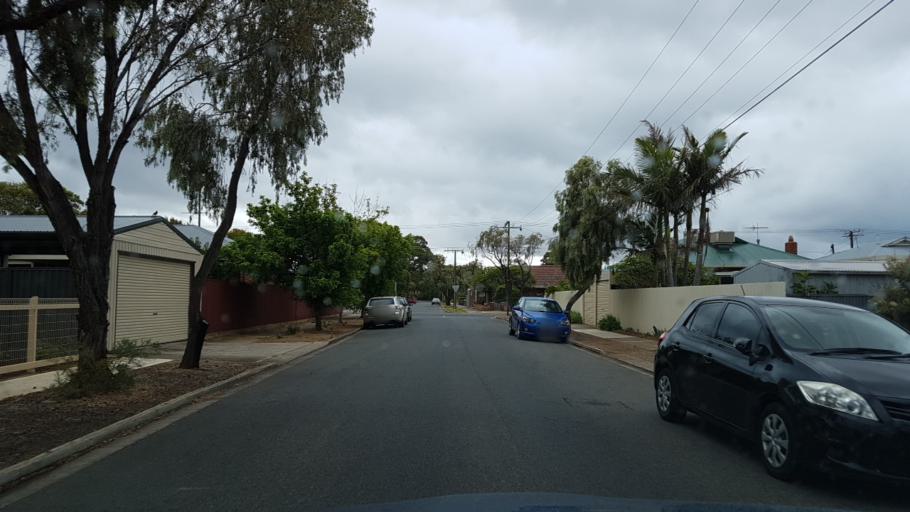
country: AU
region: South Australia
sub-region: Marion
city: South Plympton
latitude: -34.9713
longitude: 138.5542
